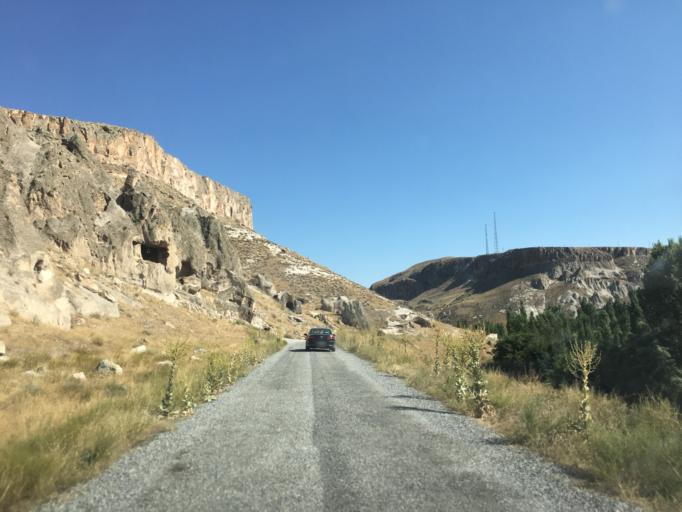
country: TR
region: Kayseri
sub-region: Yesilhisar
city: Yesilhisar
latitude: 38.3488
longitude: 34.9693
